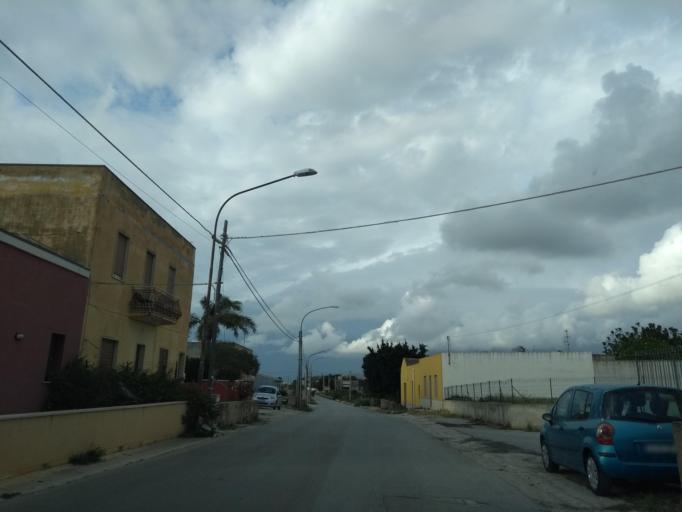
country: IT
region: Sicily
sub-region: Trapani
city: Marausa
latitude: 37.9532
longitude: 12.5155
